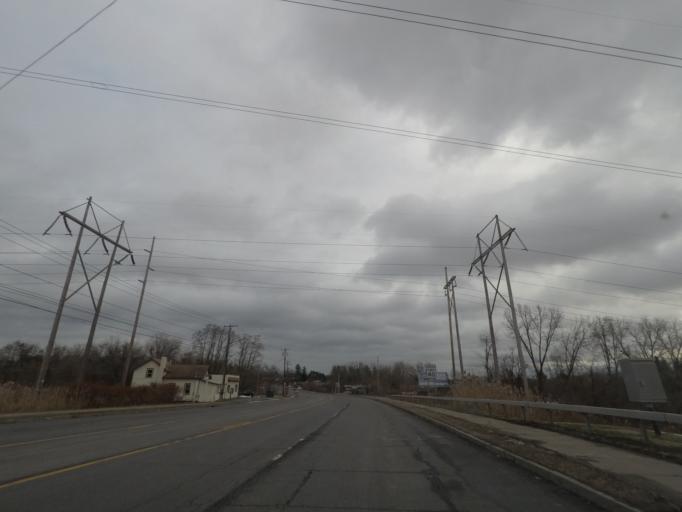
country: US
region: New York
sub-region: Rensselaer County
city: Hampton Manor
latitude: 42.6092
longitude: -73.7253
